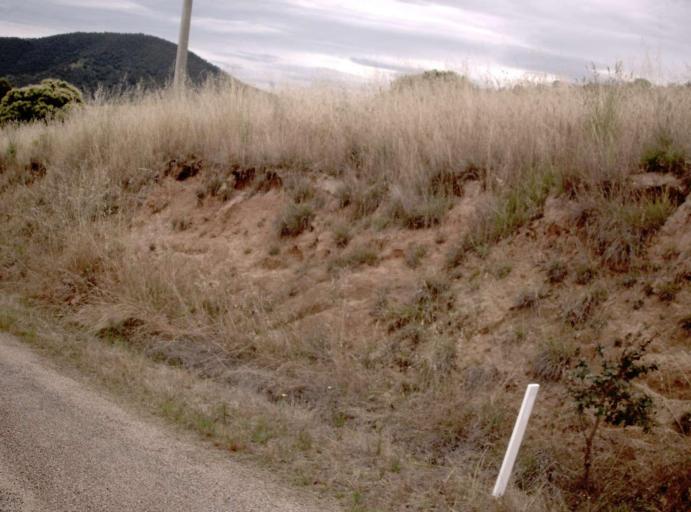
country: AU
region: Victoria
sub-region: East Gippsland
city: Bairnsdale
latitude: -37.4718
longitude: 147.2455
